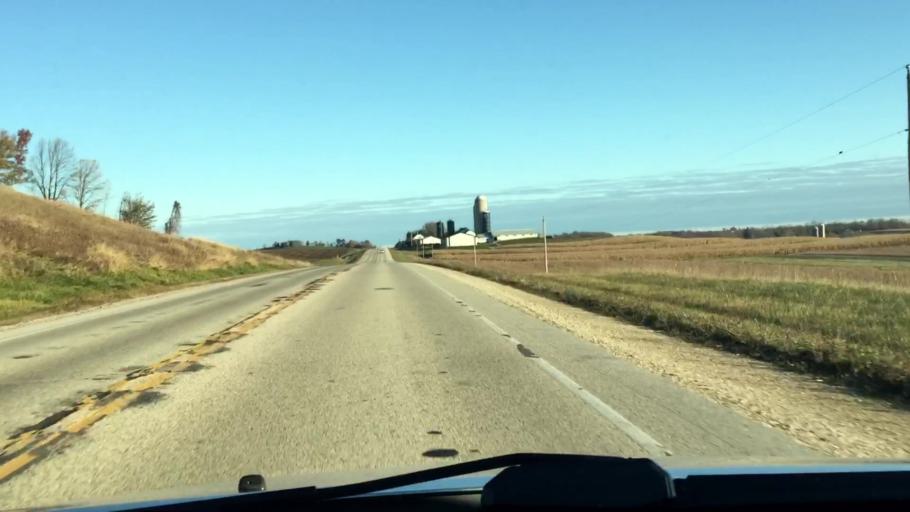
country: US
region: Wisconsin
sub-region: Dodge County
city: Theresa
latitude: 43.4484
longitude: -88.4504
